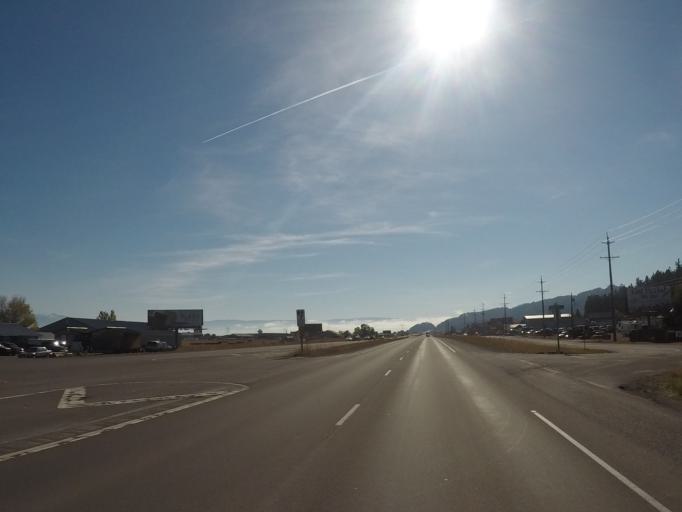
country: US
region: Montana
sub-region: Flathead County
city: Somers
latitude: 48.1232
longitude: -114.2605
